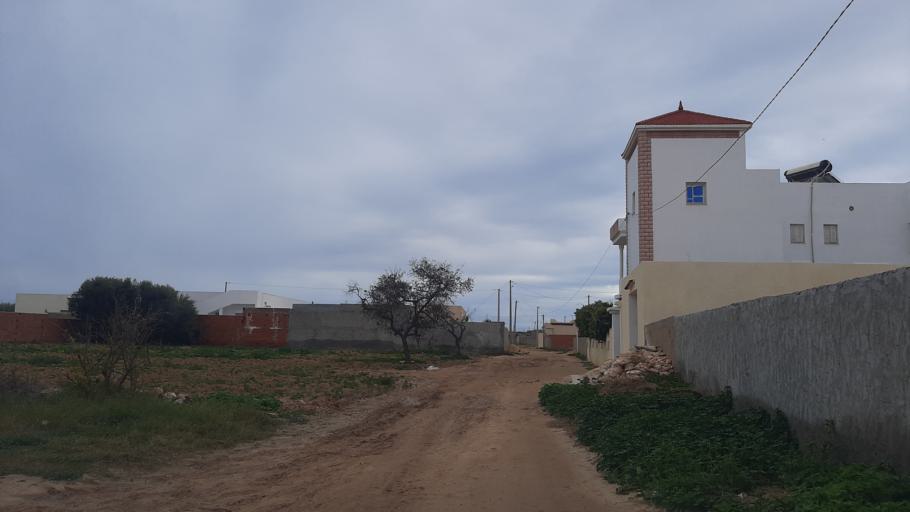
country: TN
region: Safaqis
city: Al Qarmadah
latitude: 34.7984
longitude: 10.8550
